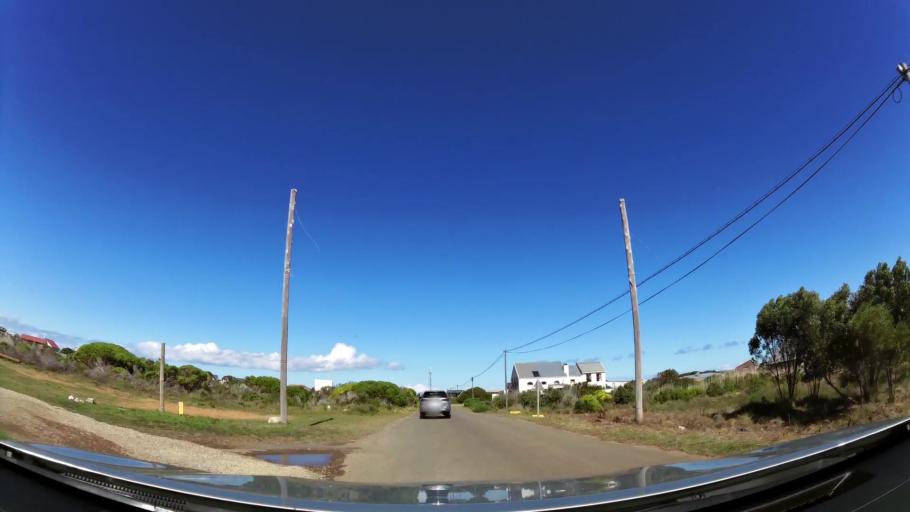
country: ZA
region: Western Cape
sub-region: Overberg District Municipality
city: Grabouw
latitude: -34.3677
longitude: 18.8911
